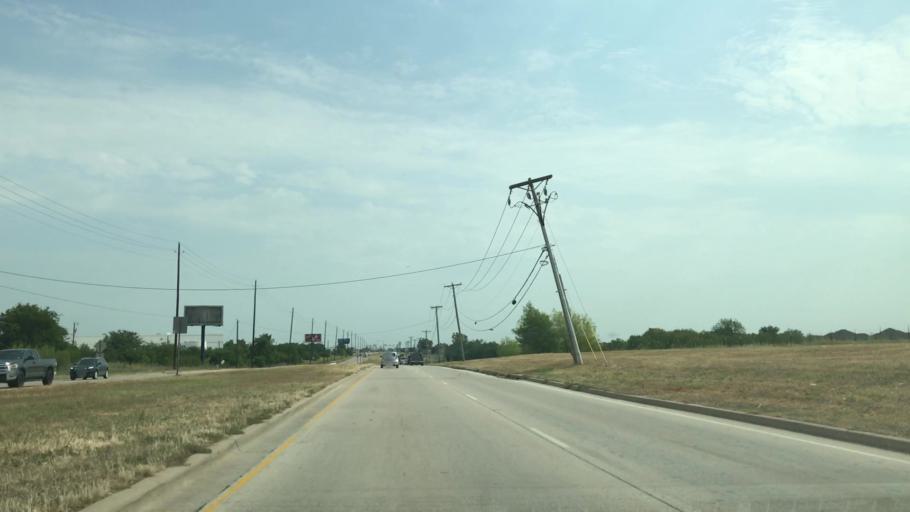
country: US
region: Texas
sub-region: Tarrant County
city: Keller
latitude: 32.9638
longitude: -97.2499
